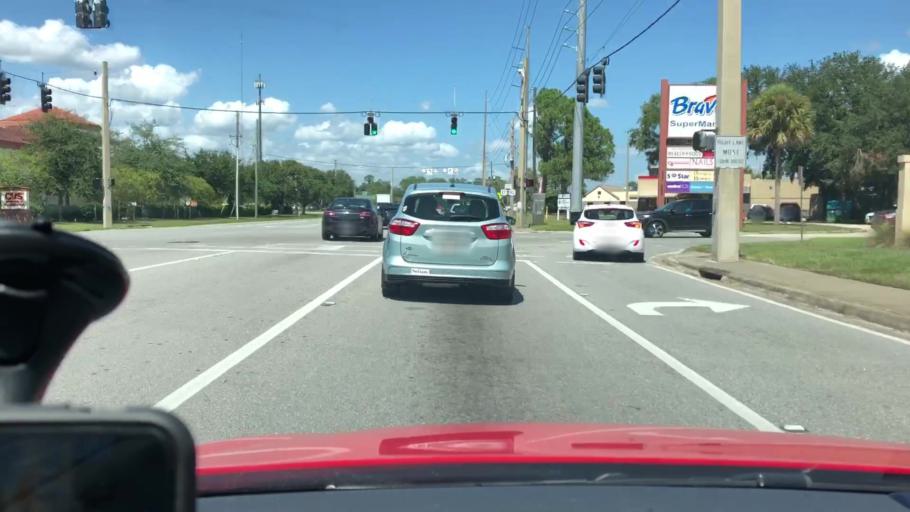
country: US
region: Florida
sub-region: Volusia County
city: Orange City
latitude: 28.9216
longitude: -81.2979
